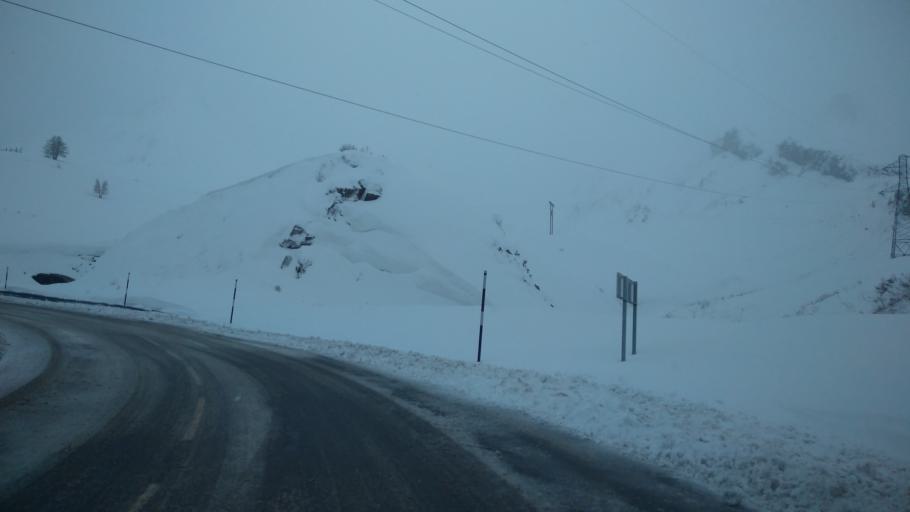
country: FR
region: Provence-Alpes-Cote d'Azur
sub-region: Departement des Hautes-Alpes
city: Le Monetier-les-Bains
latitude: 45.0428
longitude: 6.4171
